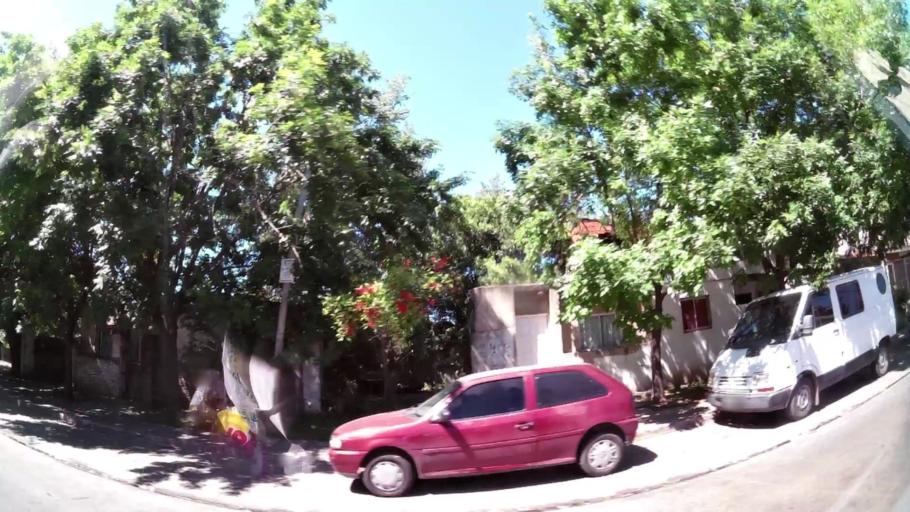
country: AR
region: Buenos Aires
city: Hurlingham
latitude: -34.5022
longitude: -58.6410
